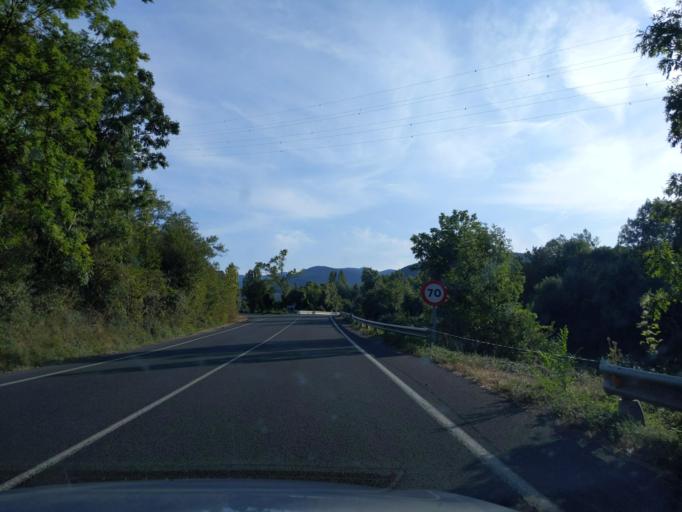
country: ES
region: La Rioja
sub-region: Provincia de La Rioja
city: Ojacastro
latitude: 42.3537
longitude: -2.9940
